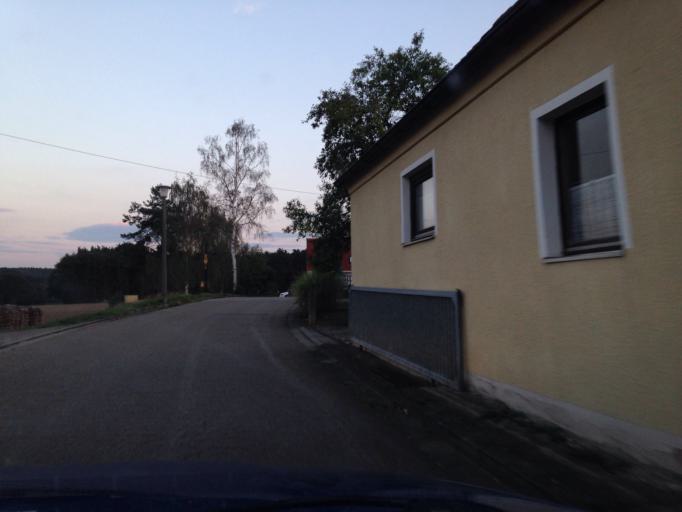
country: DE
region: Bavaria
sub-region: Regierungsbezirk Mittelfranken
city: Hilpoltstein
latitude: 49.1562
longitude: 11.1733
